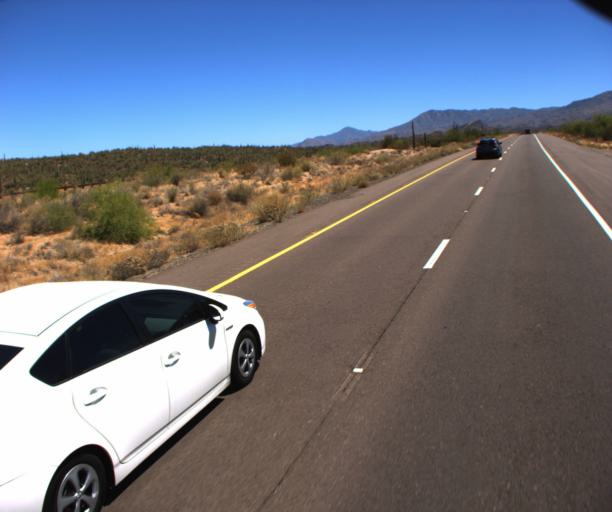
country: US
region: Arizona
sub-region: Maricopa County
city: Rio Verde
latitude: 33.6595
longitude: -111.5196
